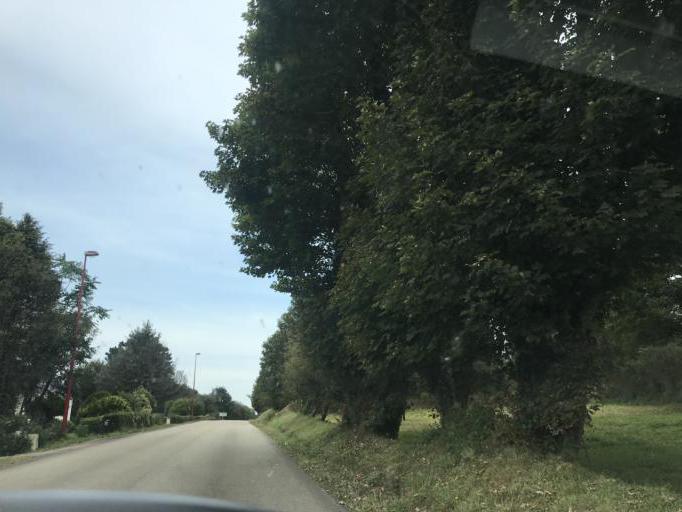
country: FR
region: Brittany
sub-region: Departement du Finistere
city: Plouneour-Menez
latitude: 48.3644
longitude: -3.8505
